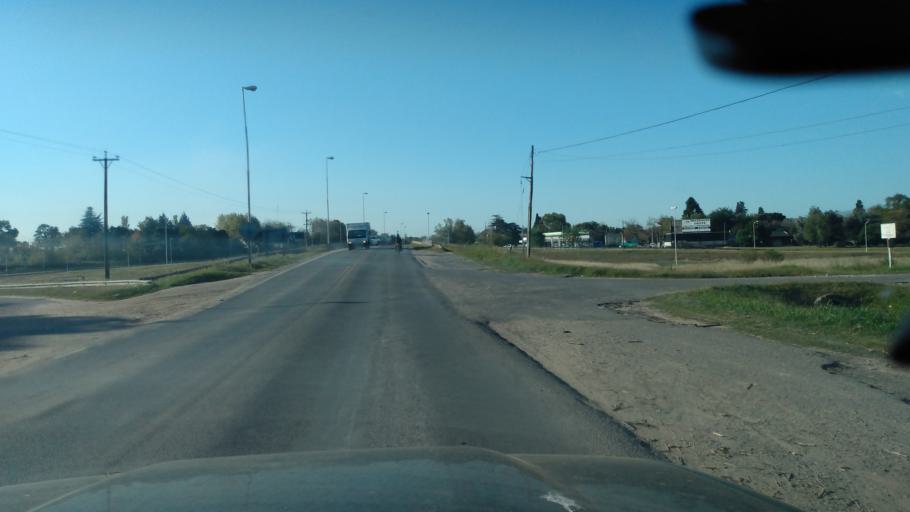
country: AR
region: Buenos Aires
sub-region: Partido de Lujan
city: Lujan
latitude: -34.5473
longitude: -59.1240
